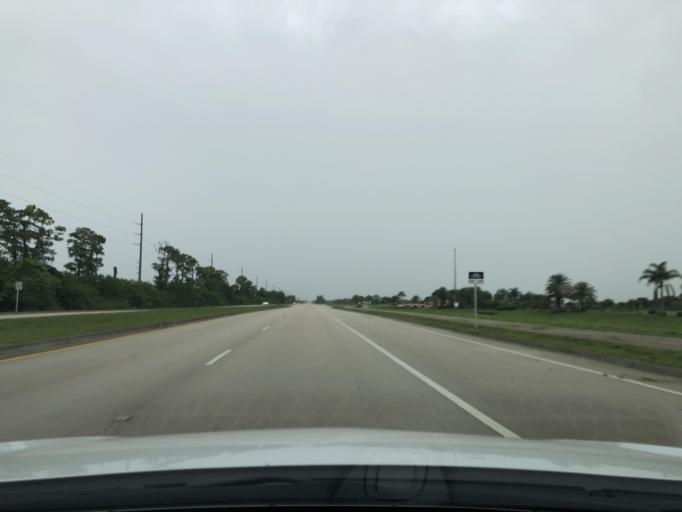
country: US
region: Florida
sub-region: Collier County
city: Immokalee
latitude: 26.2949
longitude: -81.4280
